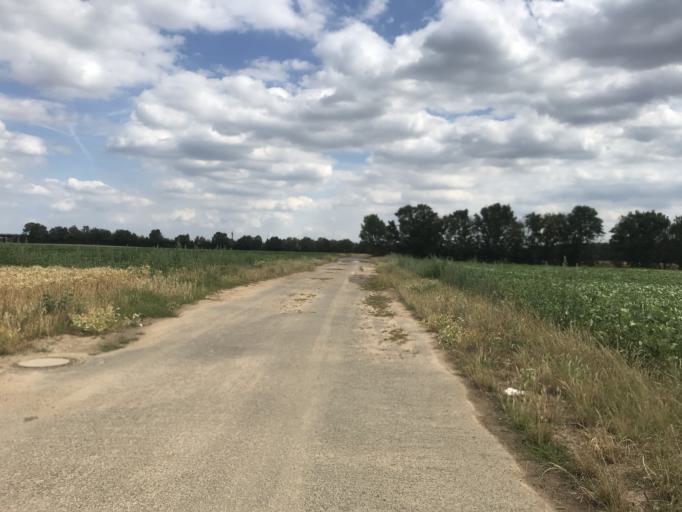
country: DE
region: Hesse
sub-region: Regierungsbezirk Darmstadt
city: Wiesbaden
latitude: 50.0460
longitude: 8.2920
